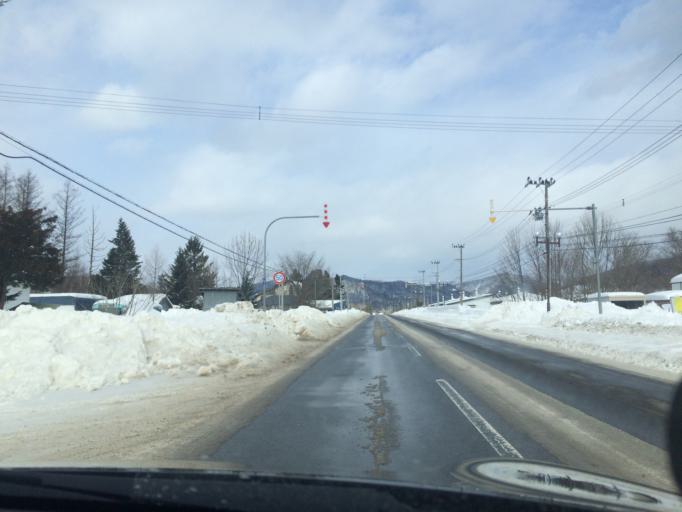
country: JP
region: Hokkaido
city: Shimo-furano
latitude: 42.9891
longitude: 142.3991
